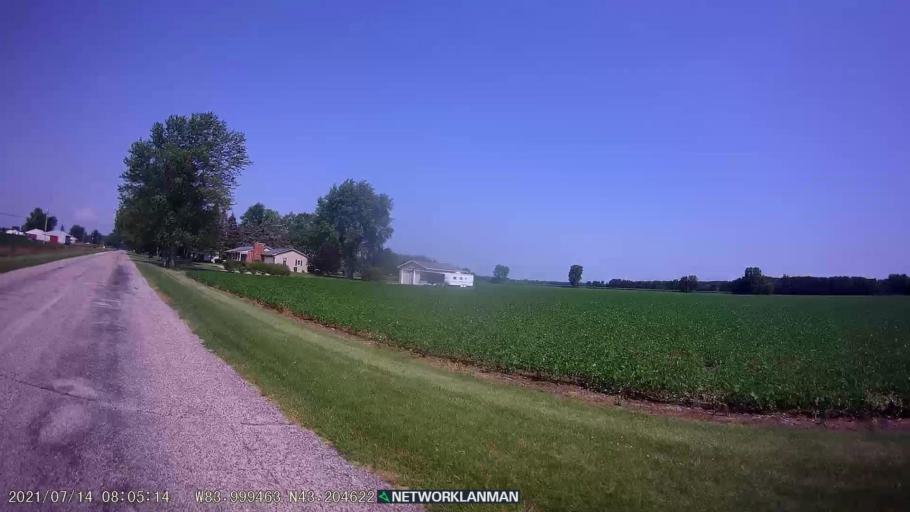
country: US
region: Michigan
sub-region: Saginaw County
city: Burt
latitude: 43.2046
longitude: -83.9998
